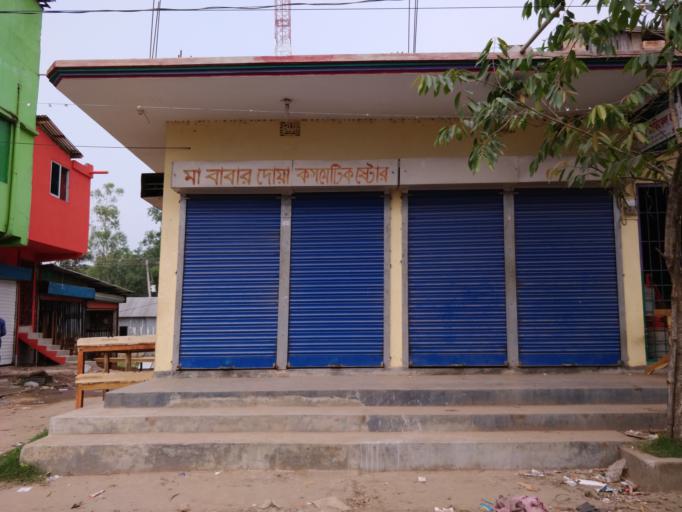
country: BD
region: Sylhet
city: Habiganj
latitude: 24.1685
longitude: 91.3546
